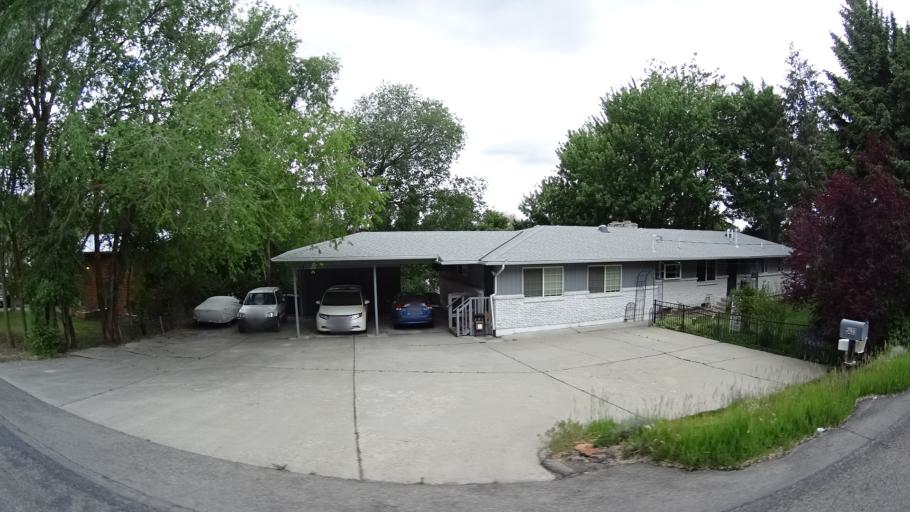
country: US
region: Idaho
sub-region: Ada County
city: Garden City
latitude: 43.6727
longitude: -116.2567
